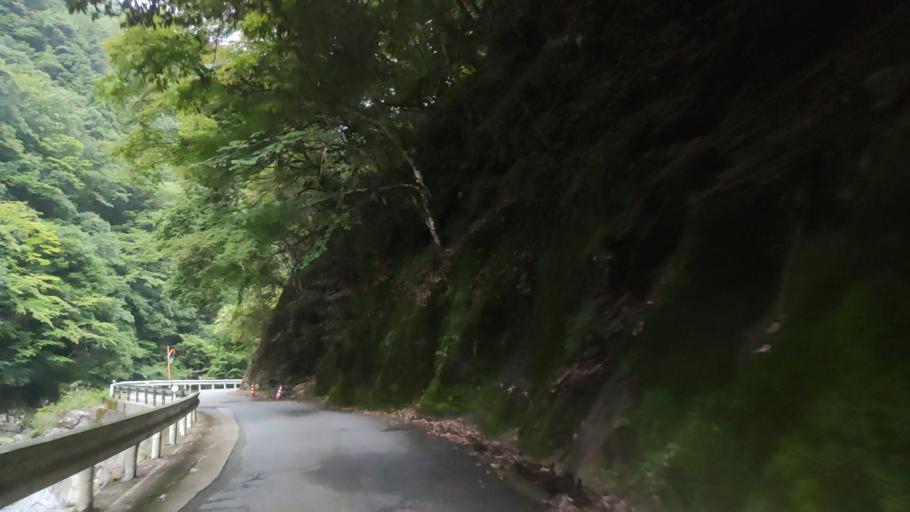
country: JP
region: Wakayama
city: Koya
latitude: 34.2507
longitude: 135.6534
